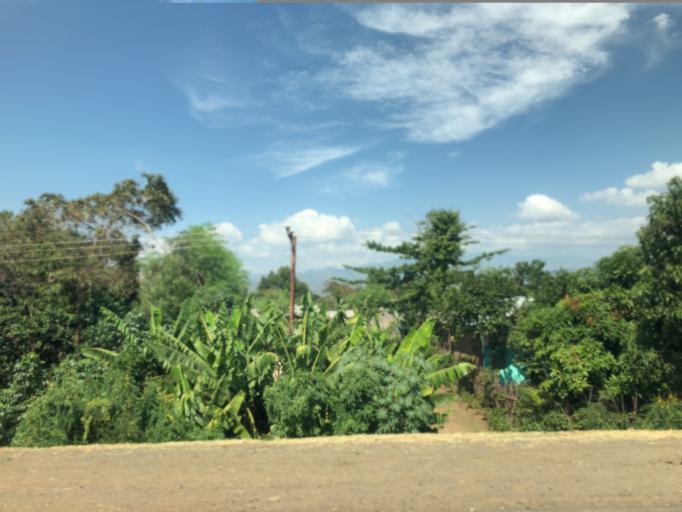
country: ET
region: Southern Nations, Nationalities, and People's Region
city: Arba Minch'
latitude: 5.8504
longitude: 37.4682
